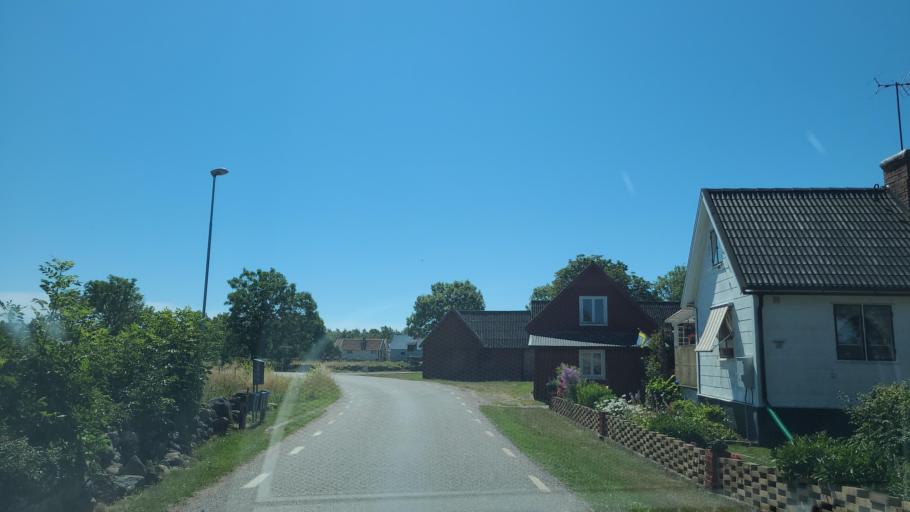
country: SE
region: Kalmar
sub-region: Borgholms Kommun
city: Borgholm
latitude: 56.7445
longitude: 16.6667
